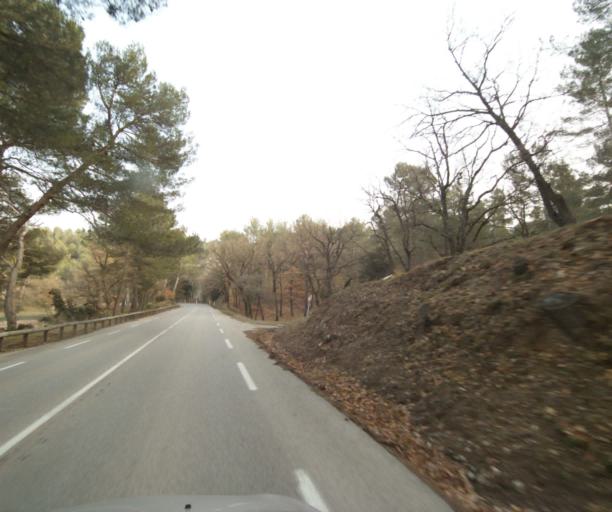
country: FR
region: Provence-Alpes-Cote d'Azur
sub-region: Departement du Vaucluse
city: Cadenet
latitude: 43.7051
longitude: 5.3540
